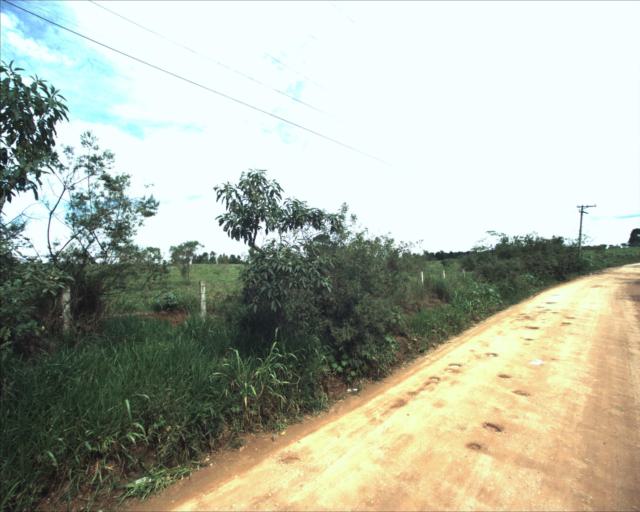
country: BR
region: Sao Paulo
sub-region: Aracoiaba Da Serra
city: Aracoiaba da Serra
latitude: -23.5580
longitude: -47.5545
